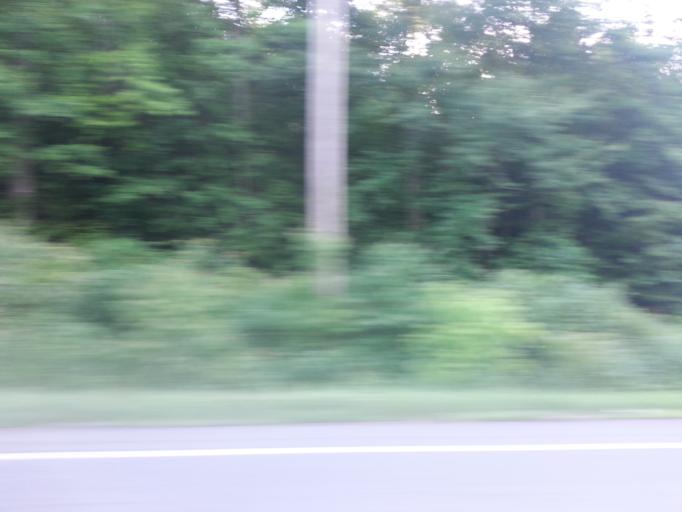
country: US
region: North Carolina
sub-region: Cherokee County
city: Murphy
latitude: 34.9932
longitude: -84.0728
